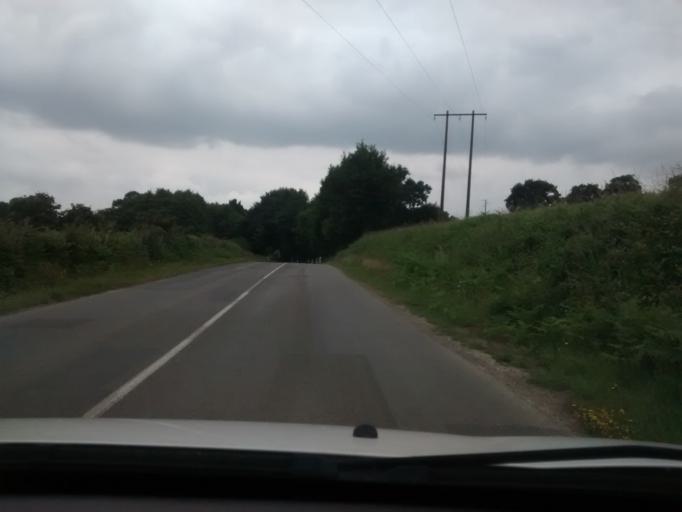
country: FR
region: Brittany
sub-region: Departement d'Ille-et-Vilaine
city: La Bouexiere
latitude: 48.1977
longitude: -1.4692
